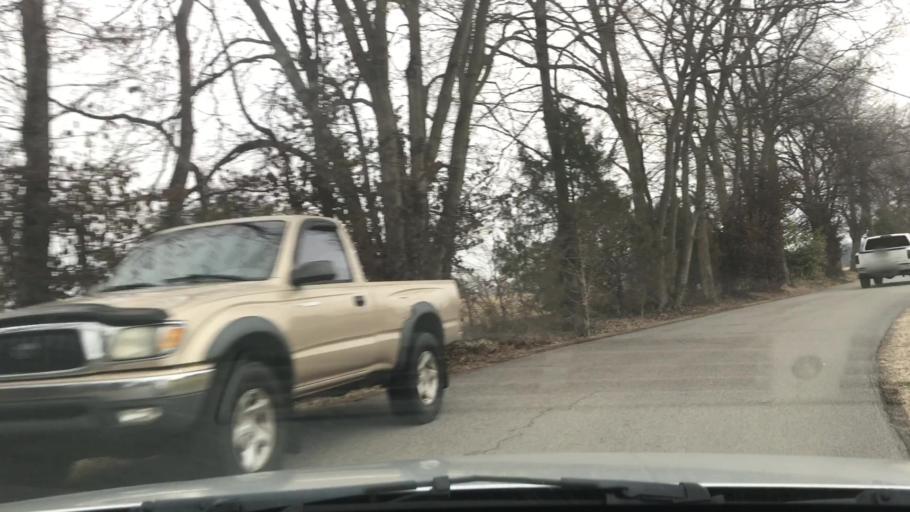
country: US
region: Kentucky
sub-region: Edmonson County
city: Brownsville
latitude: 37.0475
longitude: -86.2514
